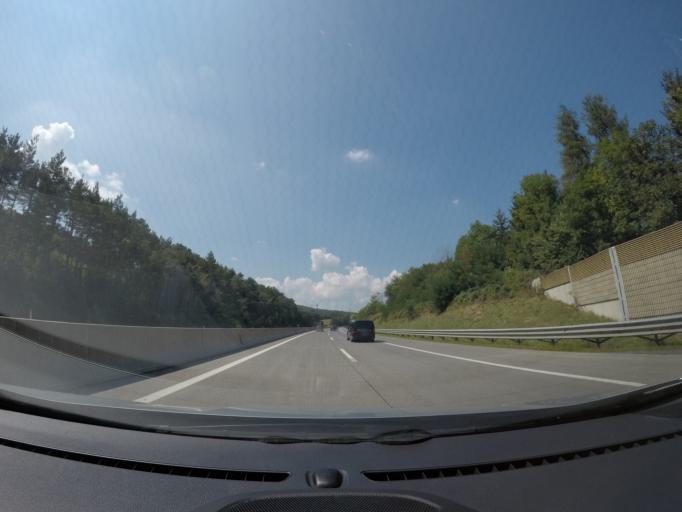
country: AT
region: Lower Austria
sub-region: Politischer Bezirk Wien-Umgebung
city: Purkersdorf
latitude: 48.1815
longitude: 16.1810
